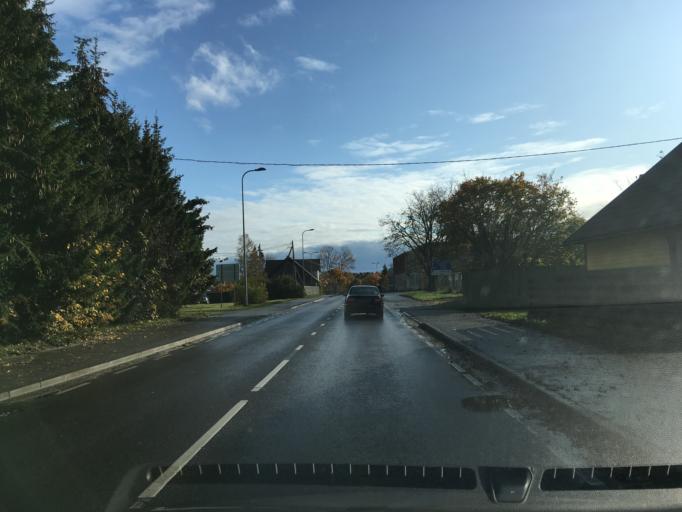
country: EE
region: Harju
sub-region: Raasiku vald
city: Raasiku
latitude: 59.1870
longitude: 25.1605
